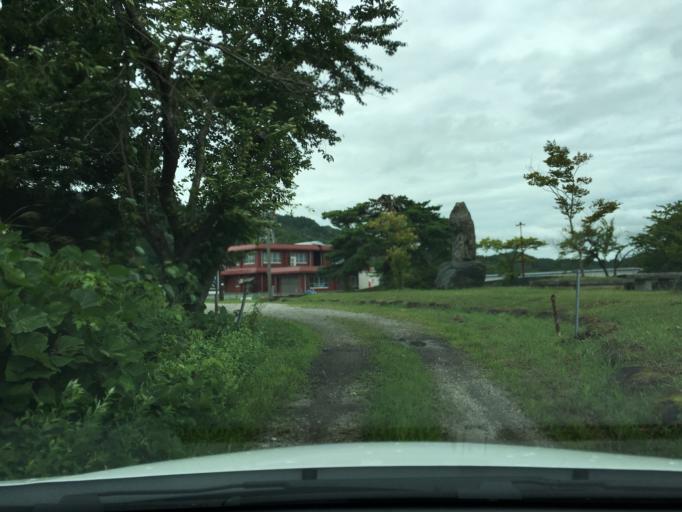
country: JP
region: Yamagata
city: Yonezawa
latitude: 37.8631
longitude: 140.1705
